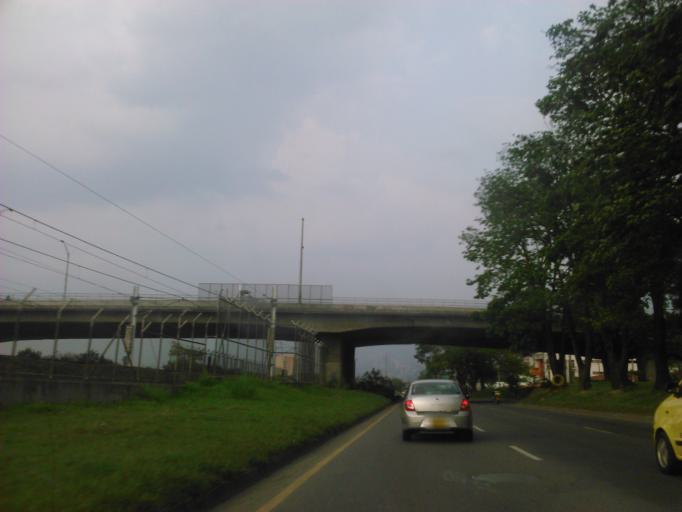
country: CO
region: Antioquia
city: Sabaneta
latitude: 6.1592
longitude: -75.6131
